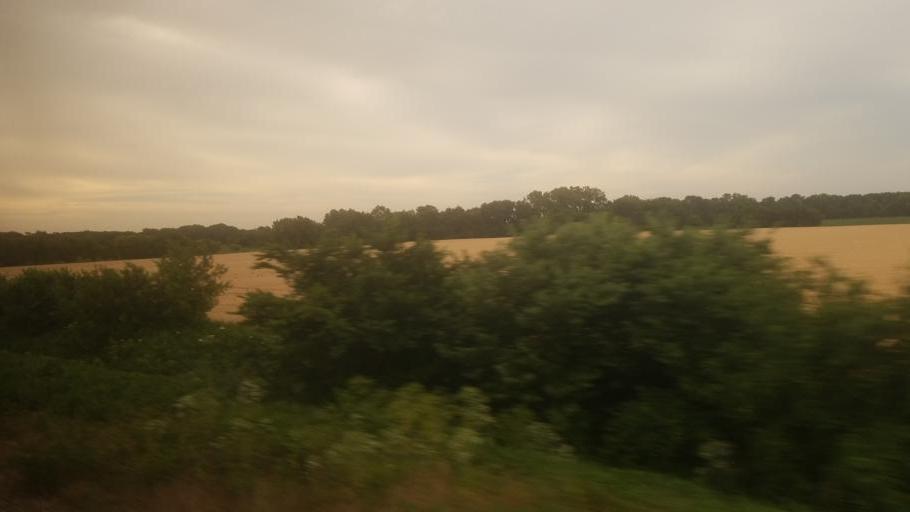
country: US
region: Kansas
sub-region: Chase County
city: Cottonwood Falls
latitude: 38.3996
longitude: -96.5677
